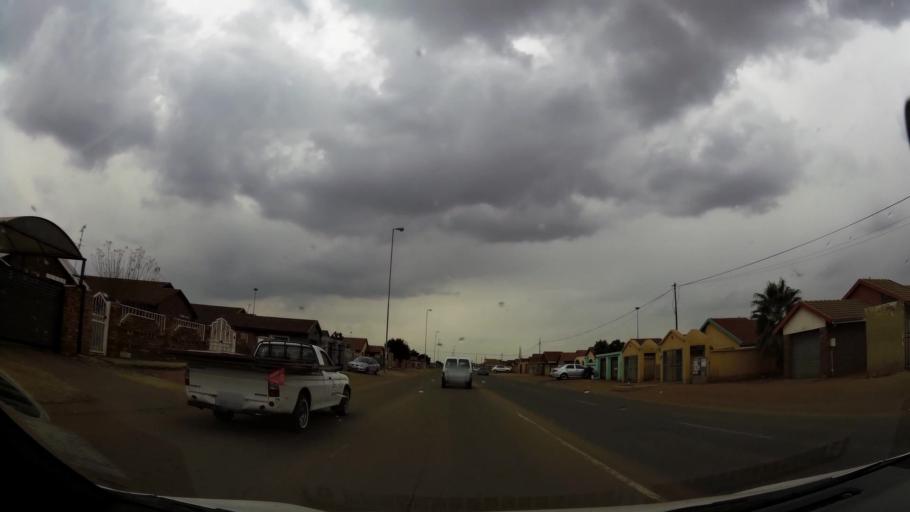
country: ZA
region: Gauteng
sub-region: Ekurhuleni Metropolitan Municipality
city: Germiston
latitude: -26.3609
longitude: 28.1499
